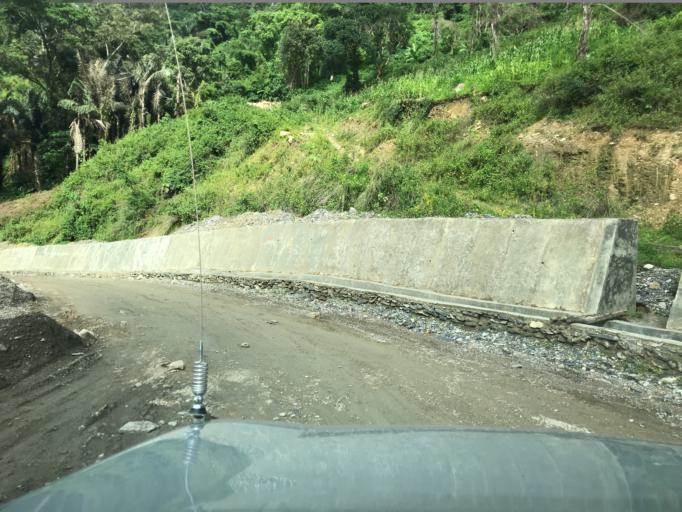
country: TL
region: Aileu
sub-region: Aileu Villa
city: Aileu
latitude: -8.6553
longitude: 125.5275
